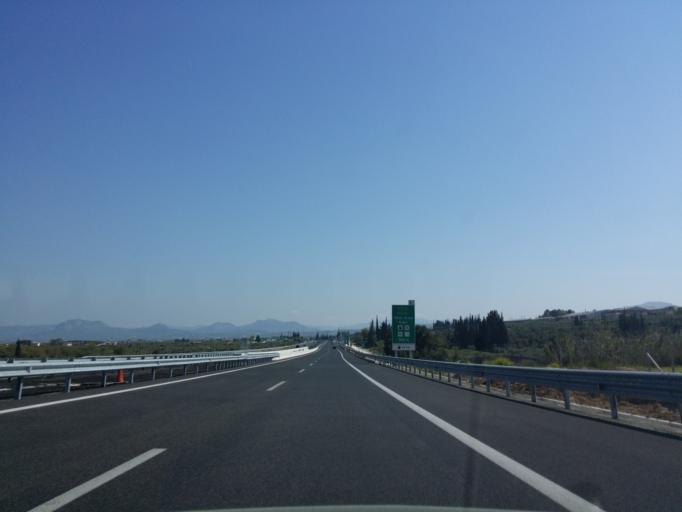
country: GR
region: Peloponnese
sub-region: Nomos Korinthias
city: Sikyon
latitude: 37.9808
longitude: 22.7367
